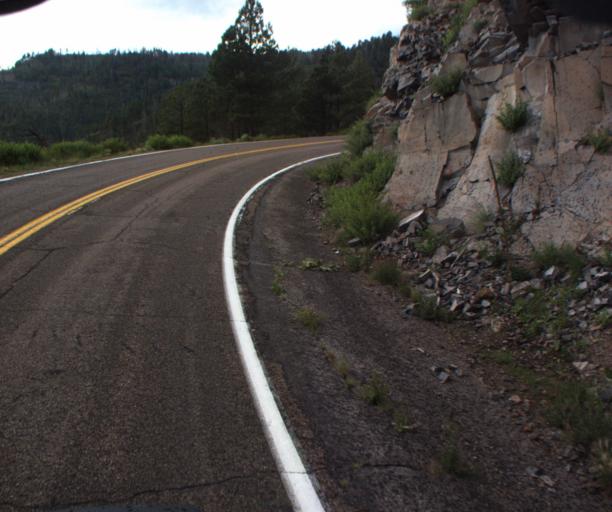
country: US
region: Arizona
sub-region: Greenlee County
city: Morenci
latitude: 33.5707
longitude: -109.3360
